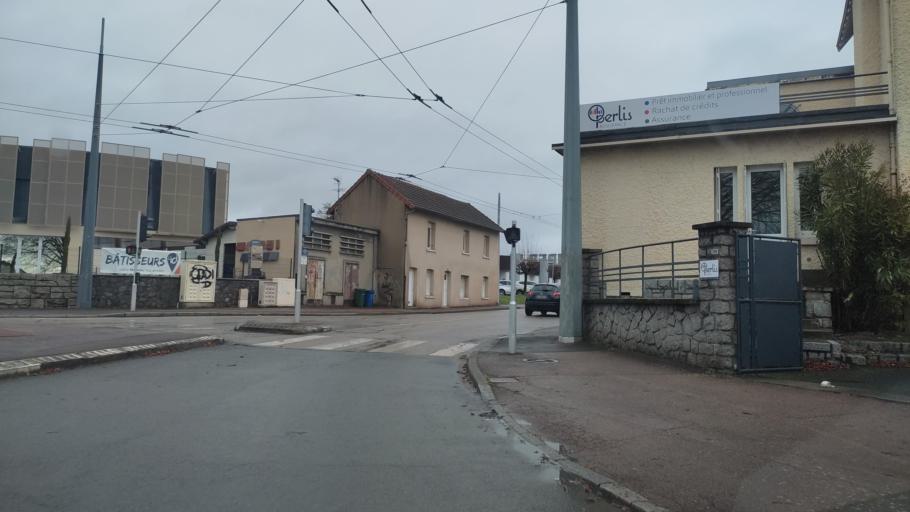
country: FR
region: Limousin
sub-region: Departement de la Haute-Vienne
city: Isle
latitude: 45.8242
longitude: 1.2263
